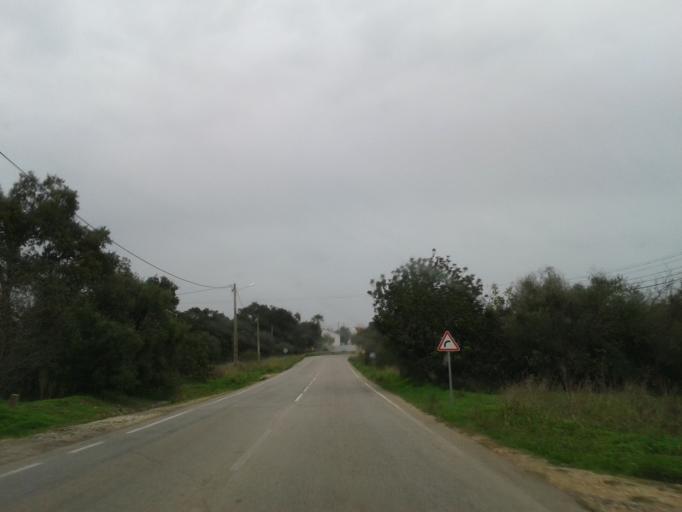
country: PT
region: Faro
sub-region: Silves
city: Silves
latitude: 37.1725
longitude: -8.4110
